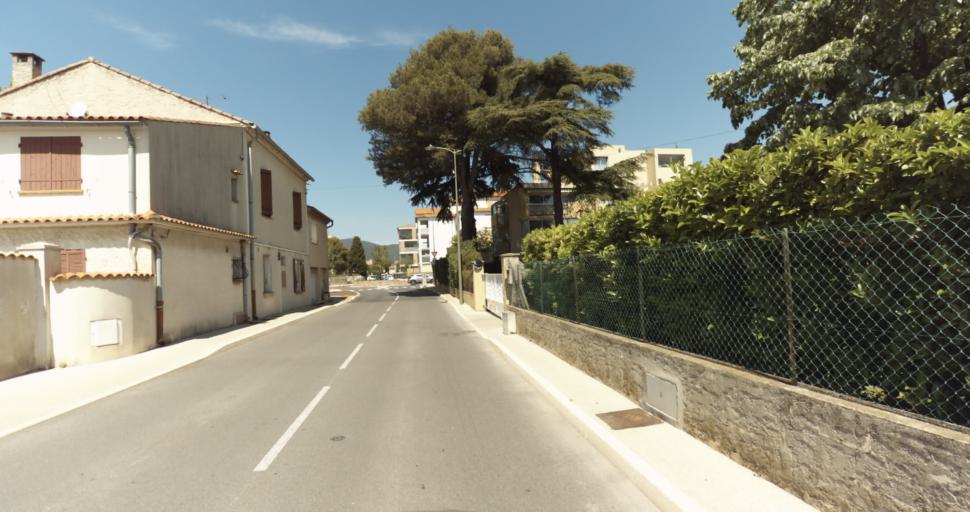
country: FR
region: Provence-Alpes-Cote d'Azur
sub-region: Departement du Var
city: La Crau
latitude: 43.1463
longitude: 6.0692
